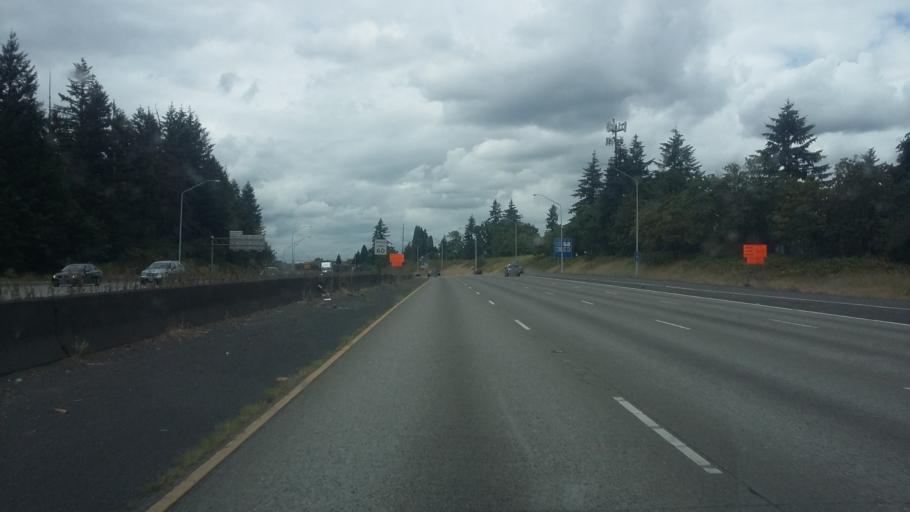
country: US
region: Washington
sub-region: Clark County
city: Orchards
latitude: 45.6097
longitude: -122.5524
